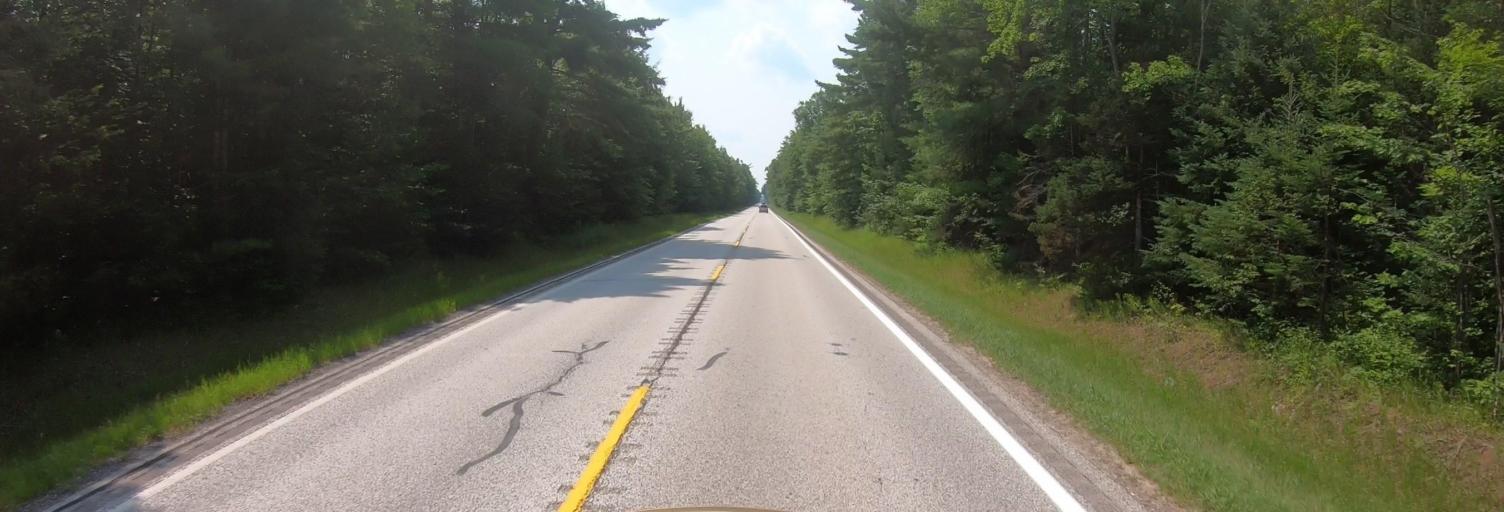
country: US
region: Michigan
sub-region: Luce County
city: Newberry
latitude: 46.5040
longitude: -85.4267
